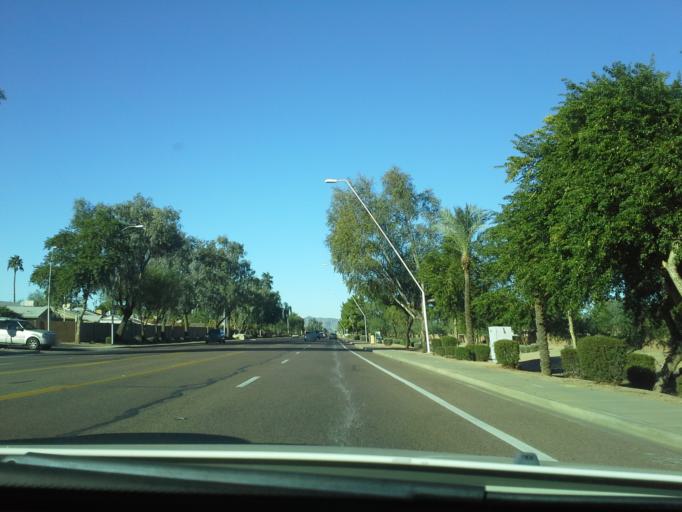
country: US
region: Arizona
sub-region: Maricopa County
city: San Carlos
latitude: 33.3498
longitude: -111.8618
